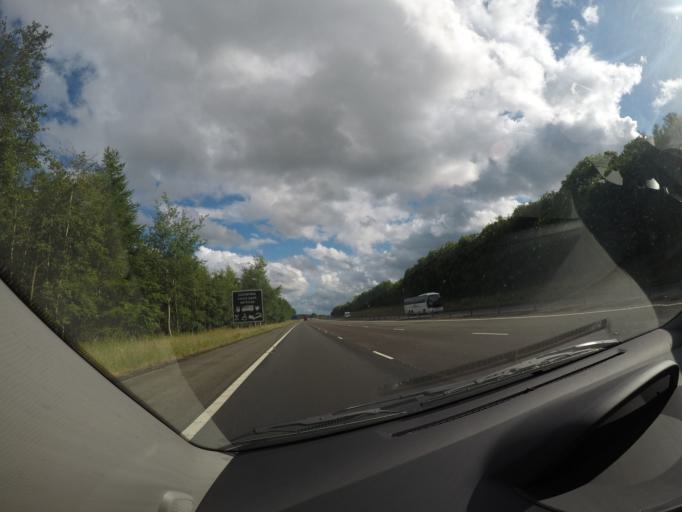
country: GB
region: Scotland
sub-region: Dumfries and Galloway
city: Moffat
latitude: 55.2498
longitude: -3.4096
